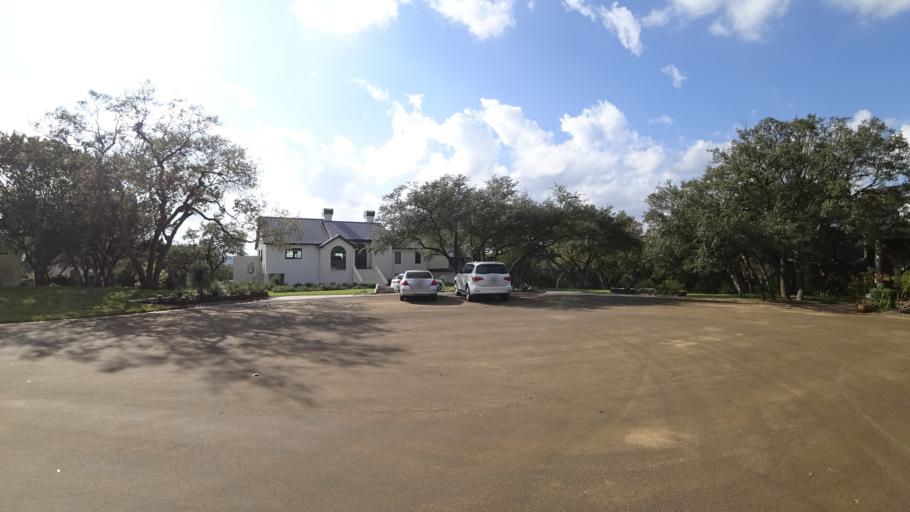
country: US
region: Texas
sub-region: Travis County
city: Lost Creek
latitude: 30.3065
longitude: -97.8467
